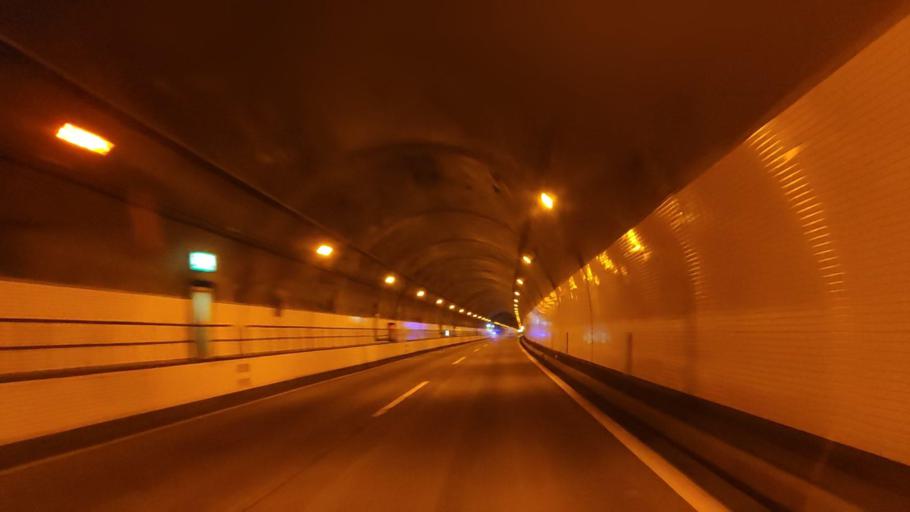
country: JP
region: Niigata
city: Itoigawa
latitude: 37.0962
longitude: 138.0000
